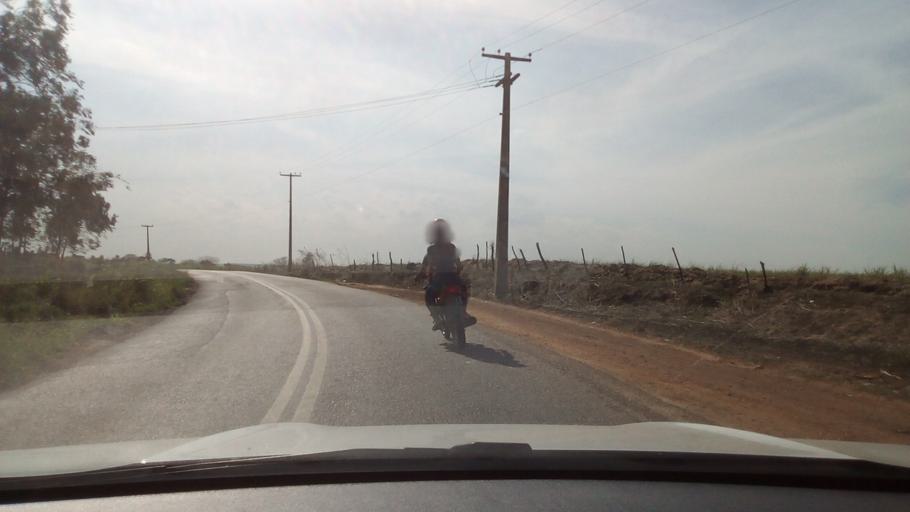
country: BR
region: Rio Grande do Norte
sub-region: Ares
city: Ares
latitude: -6.2376
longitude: -35.1733
